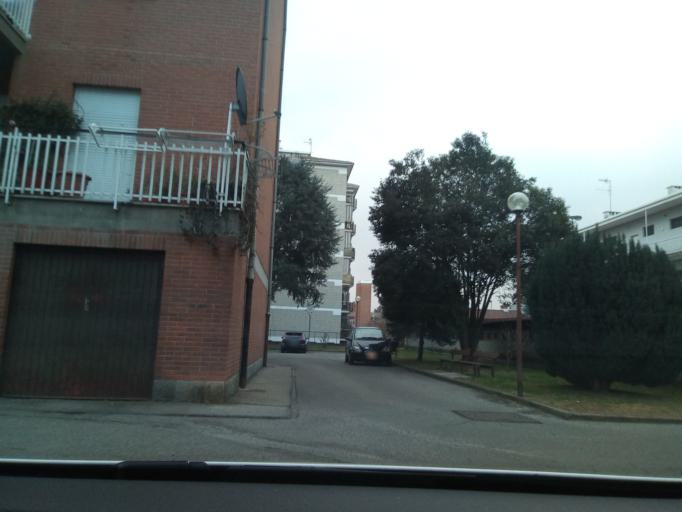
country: IT
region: Piedmont
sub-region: Provincia di Torino
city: Ivrea
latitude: 45.4527
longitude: 7.8777
